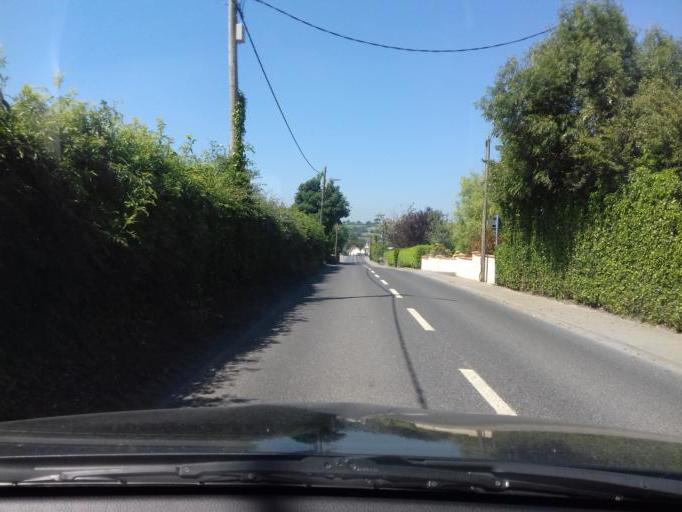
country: IE
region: Leinster
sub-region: An Mhi
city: Stamullin
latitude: 53.5829
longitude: -6.2874
